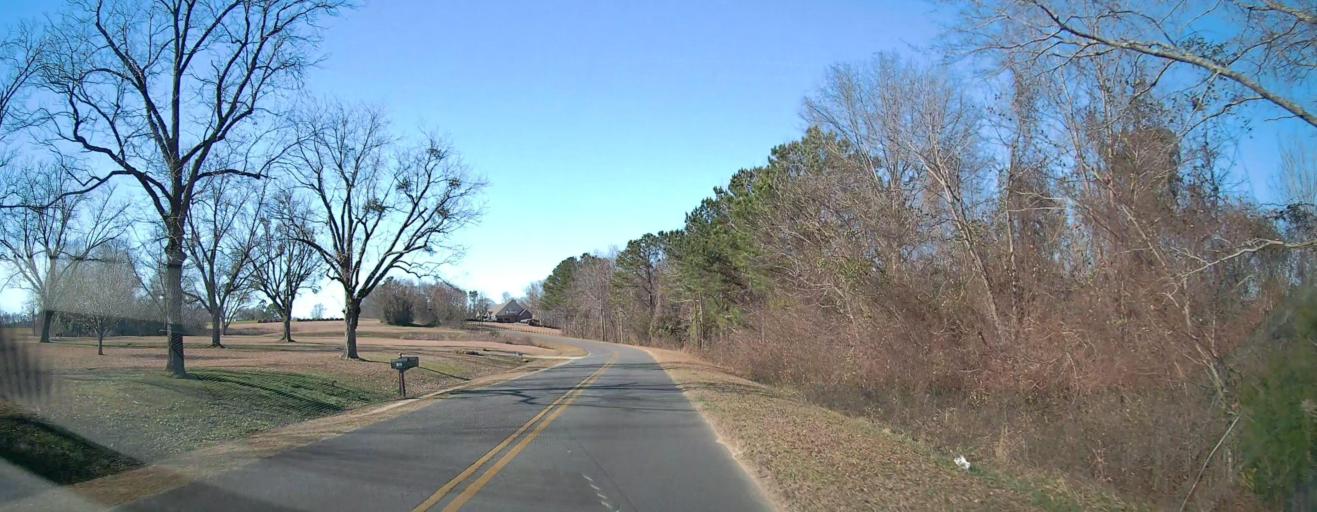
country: US
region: Georgia
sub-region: Taylor County
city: Butler
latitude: 32.6514
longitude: -84.3191
